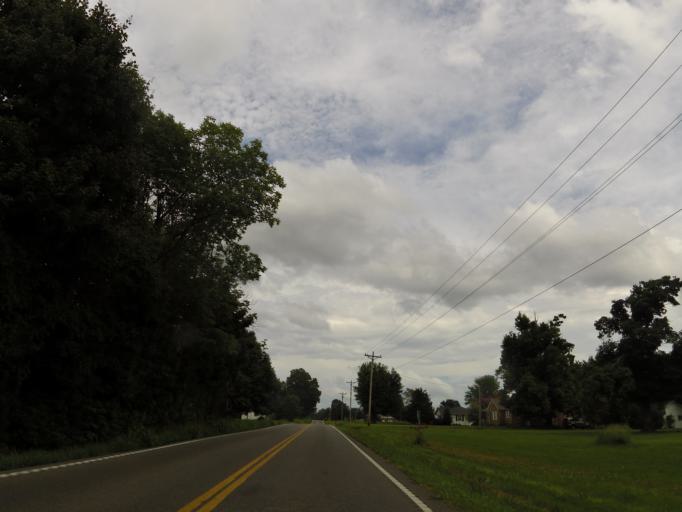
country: US
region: Kentucky
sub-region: Ballard County
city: La Center
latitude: 36.9912
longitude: -88.8941
